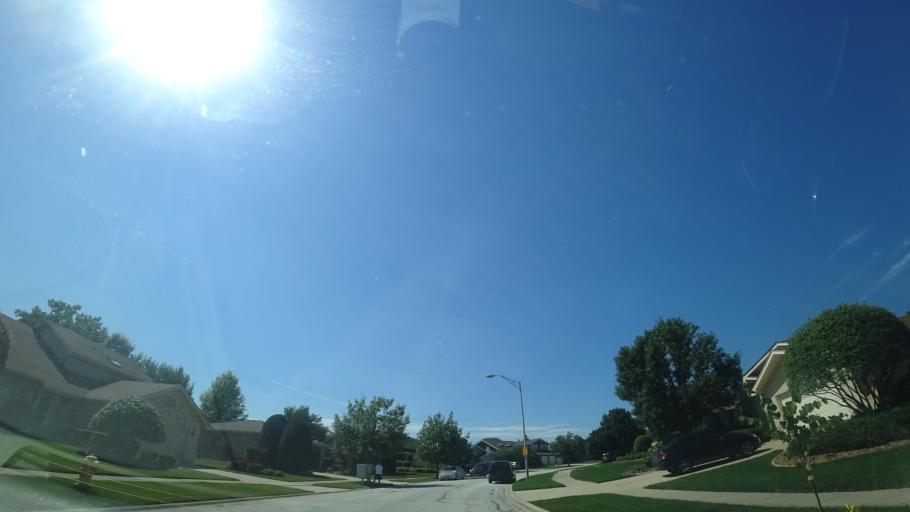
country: US
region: Illinois
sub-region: Will County
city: Mokena
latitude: 41.5662
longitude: -87.9054
